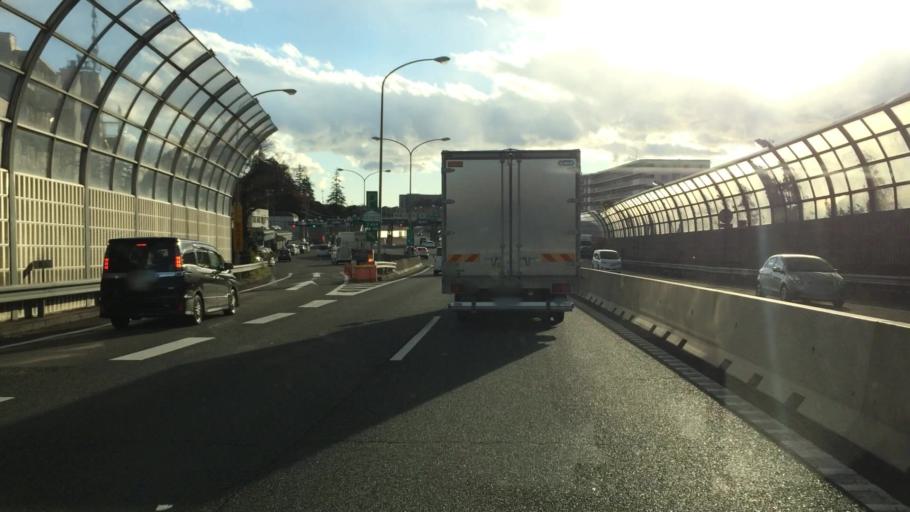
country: JP
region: Kanagawa
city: Yokohama
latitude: 35.4245
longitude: 139.5406
